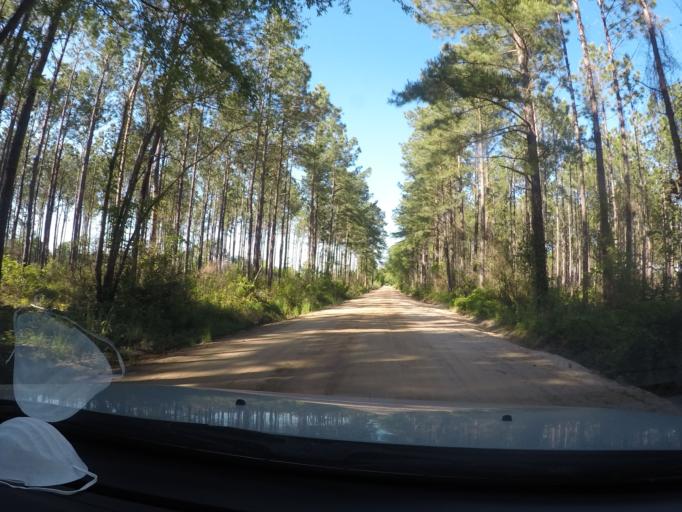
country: US
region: Georgia
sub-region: Bulloch County
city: Brooklet
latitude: 32.2906
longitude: -81.7556
